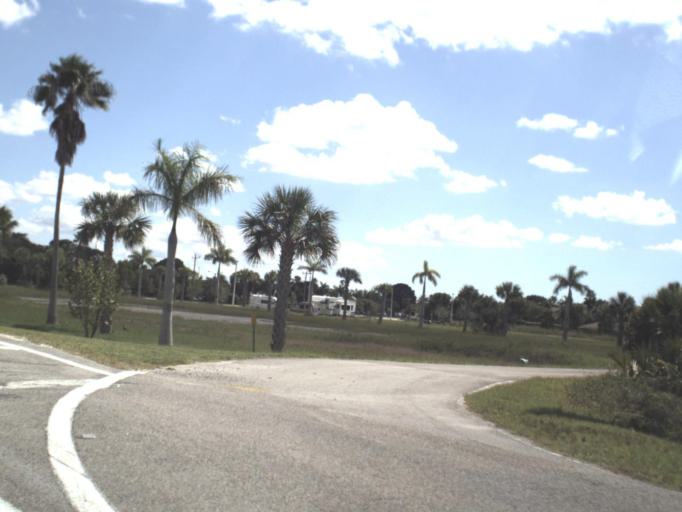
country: US
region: Florida
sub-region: Collier County
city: Marco
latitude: 25.9597
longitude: -81.5140
